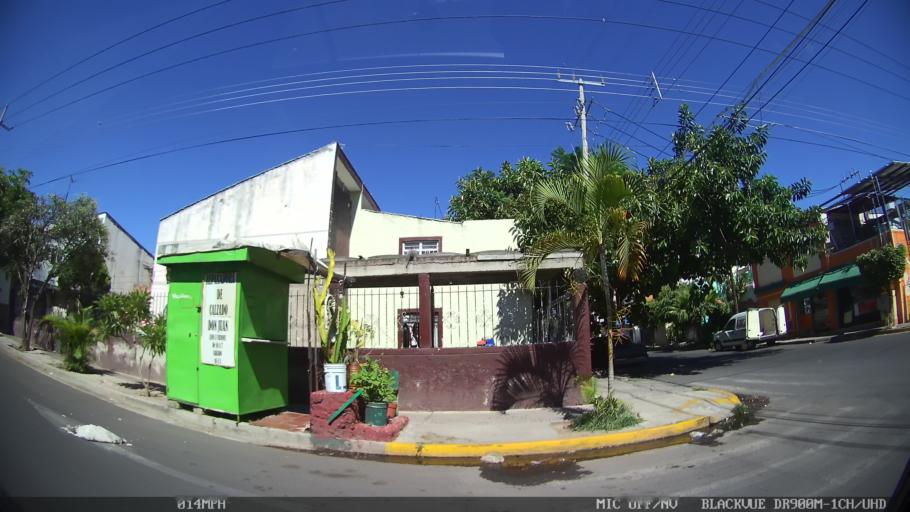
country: MX
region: Jalisco
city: Tlaquepaque
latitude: 20.6988
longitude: -103.2850
